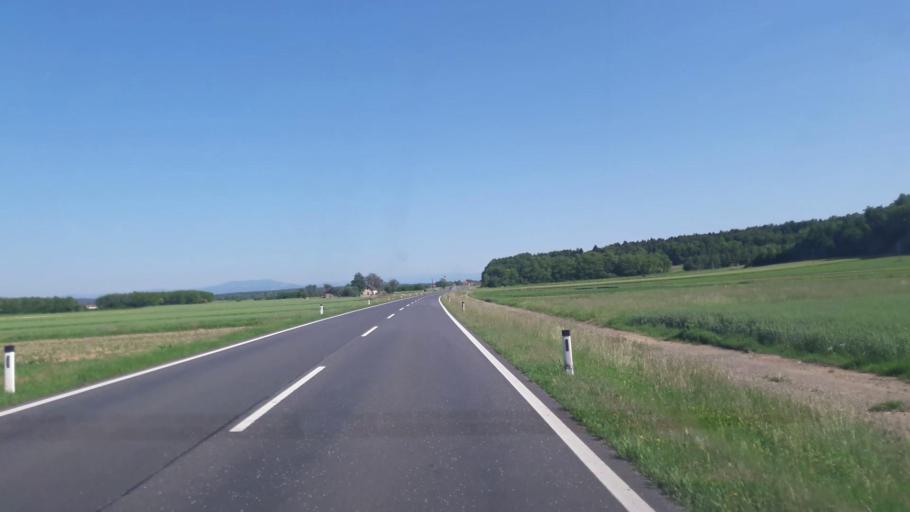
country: AT
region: Burgenland
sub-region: Politischer Bezirk Jennersdorf
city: Rudersdorf
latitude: 47.0638
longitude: 16.1151
